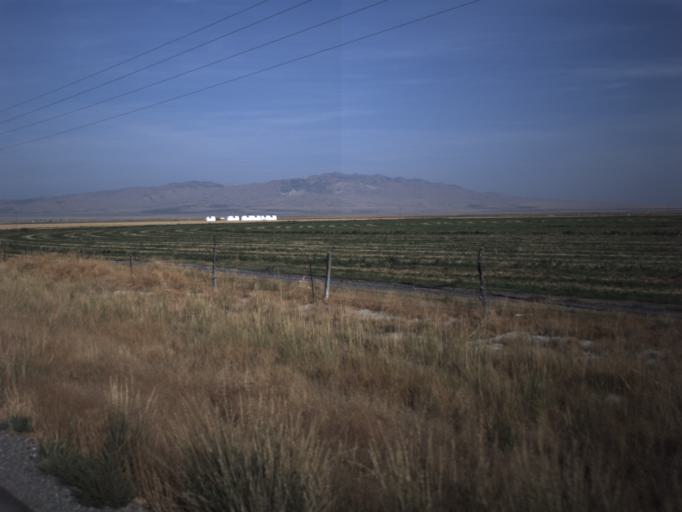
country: US
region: Idaho
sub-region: Oneida County
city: Malad City
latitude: 41.9673
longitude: -112.8375
